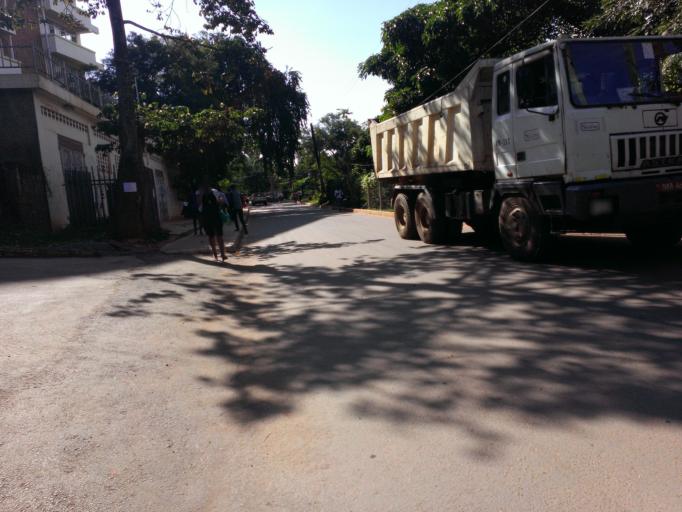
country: UG
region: Central Region
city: Kampala Central Division
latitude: 0.3320
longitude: 32.5709
